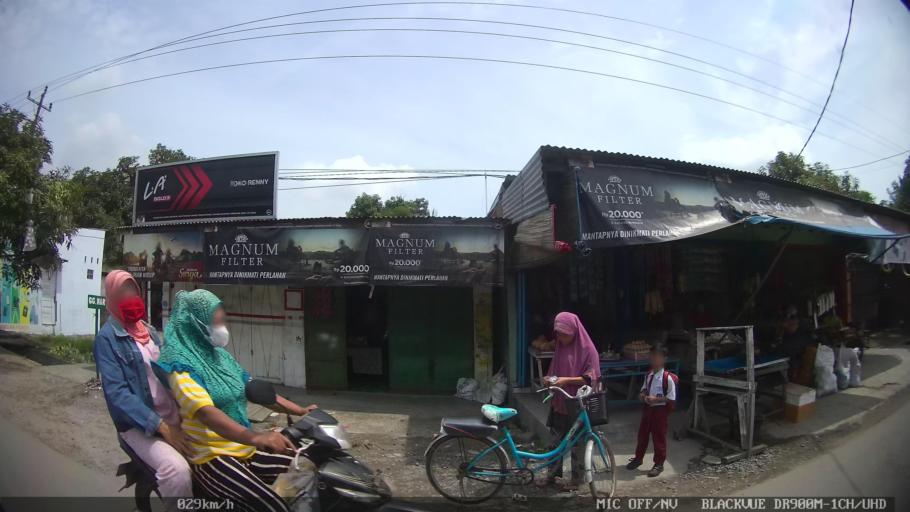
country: ID
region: North Sumatra
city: Medan
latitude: 3.6510
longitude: 98.6963
